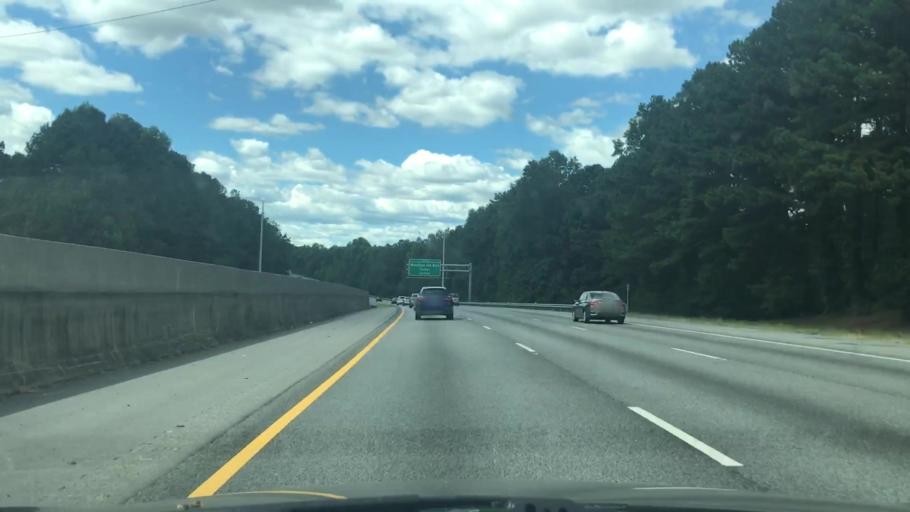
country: US
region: Georgia
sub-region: DeKalb County
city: Stone Mountain
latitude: 33.8292
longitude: -84.1787
